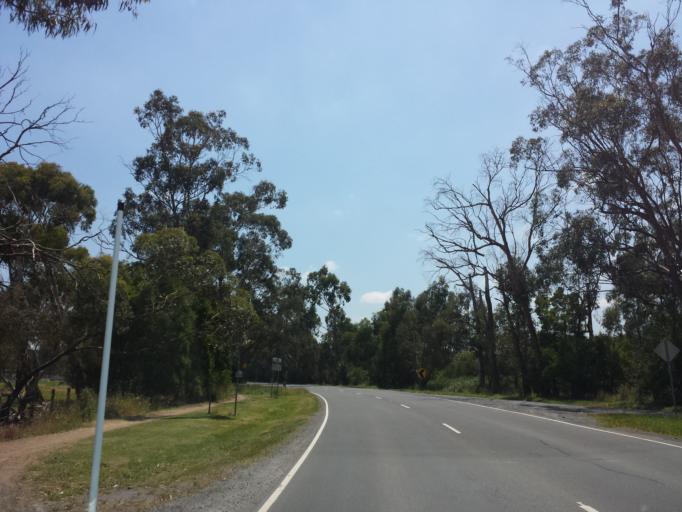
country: AU
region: Victoria
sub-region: Knox
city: The Basin
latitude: -37.8446
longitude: 145.3176
